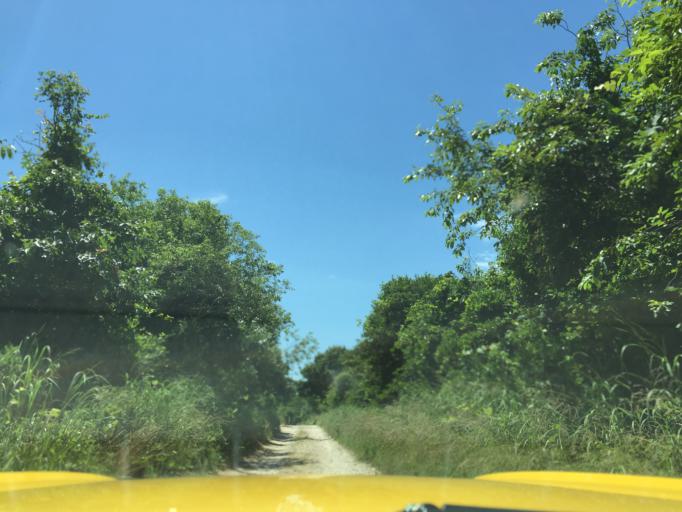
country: US
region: New York
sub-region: Suffolk County
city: Montauk
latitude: 41.0710
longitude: -71.9572
